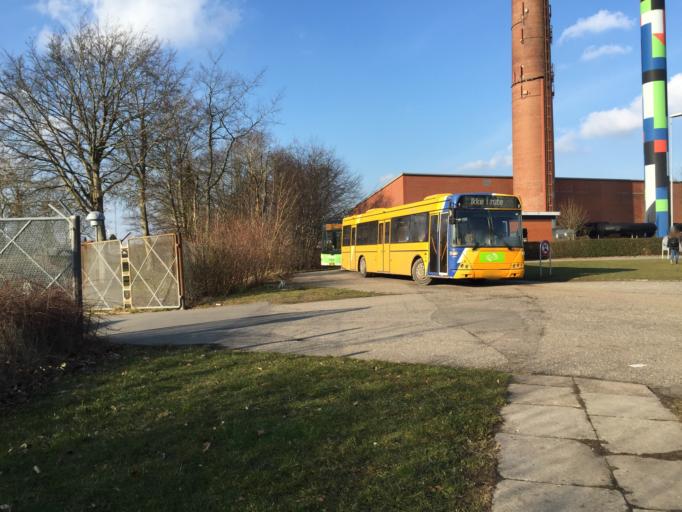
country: DK
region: South Denmark
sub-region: Odense Kommune
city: Odense
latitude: 55.3812
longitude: 10.4143
